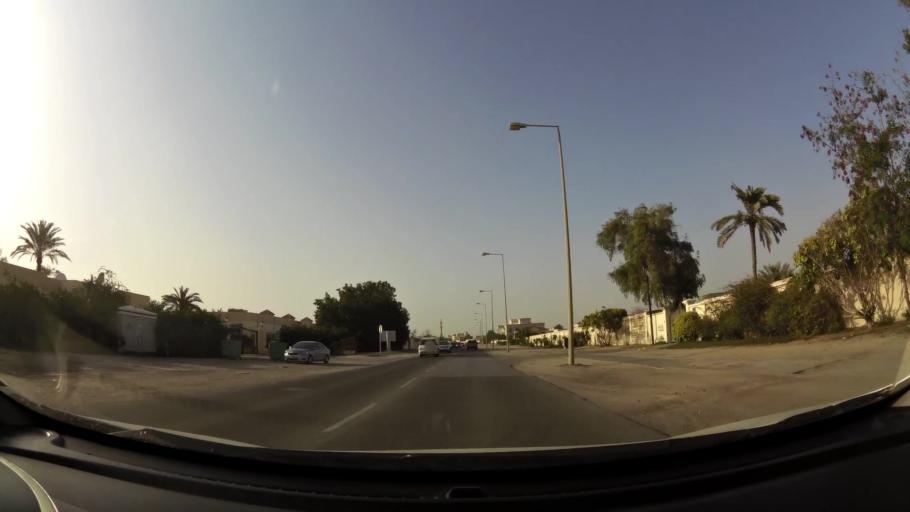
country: BH
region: Manama
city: Jidd Hafs
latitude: 26.2067
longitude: 50.4827
